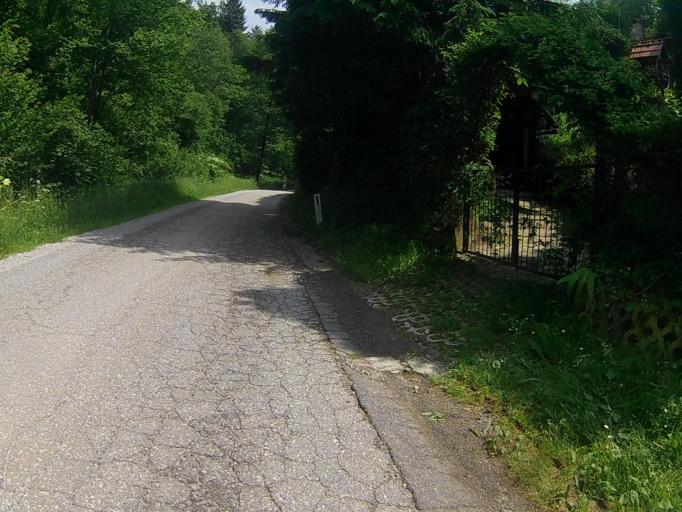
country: SI
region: Maribor
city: Kamnica
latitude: 46.5933
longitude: 15.5935
